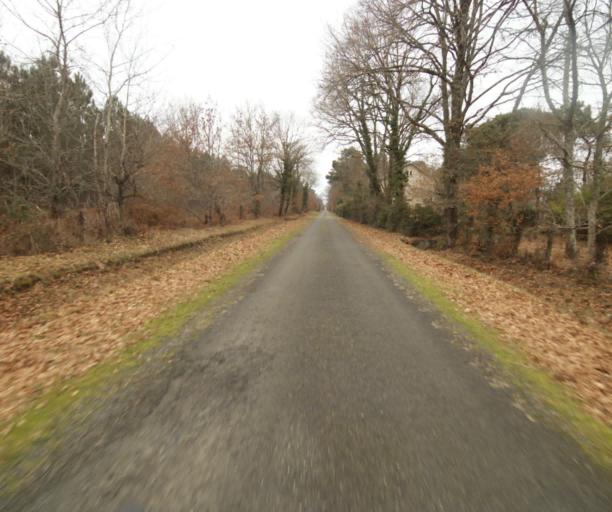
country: FR
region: Aquitaine
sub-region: Departement des Landes
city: Gabarret
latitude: 44.0438
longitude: -0.0828
